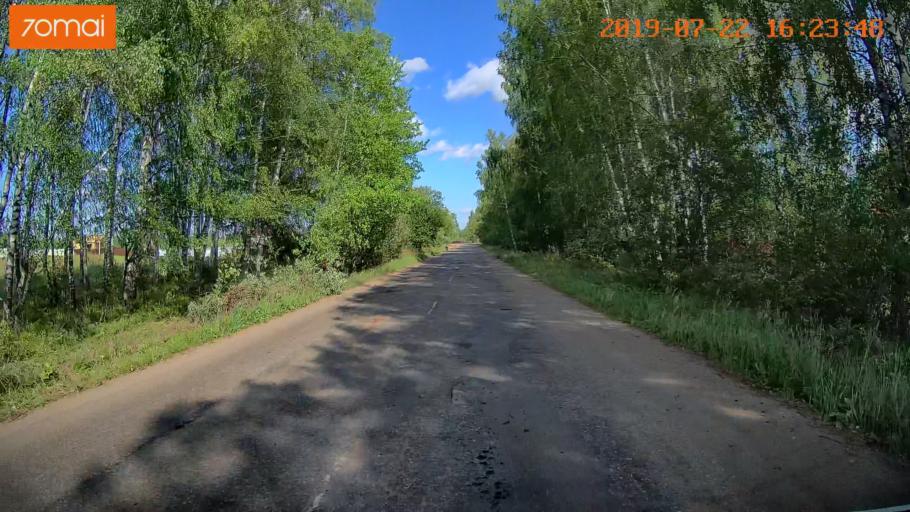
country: RU
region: Ivanovo
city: Novo-Talitsy
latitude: 57.0587
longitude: 40.9035
